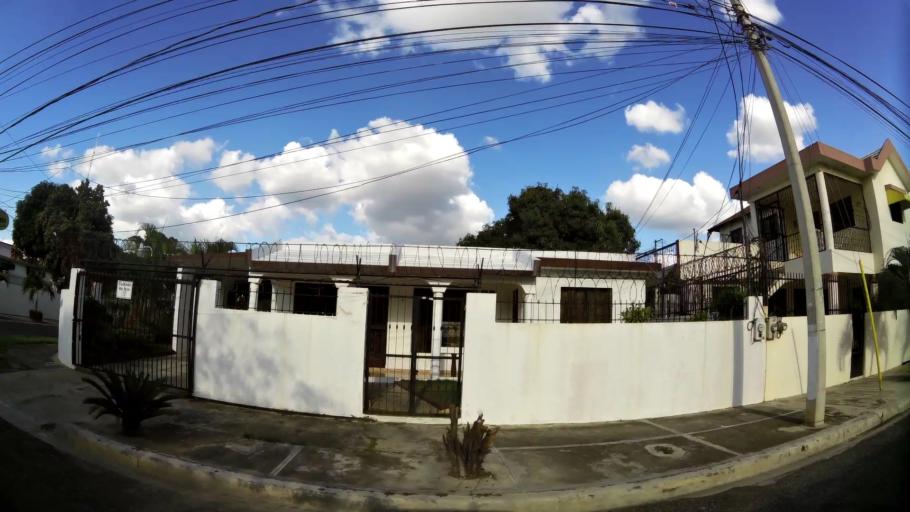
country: DO
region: Santiago
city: Santiago de los Caballeros
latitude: 19.4605
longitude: -70.6968
